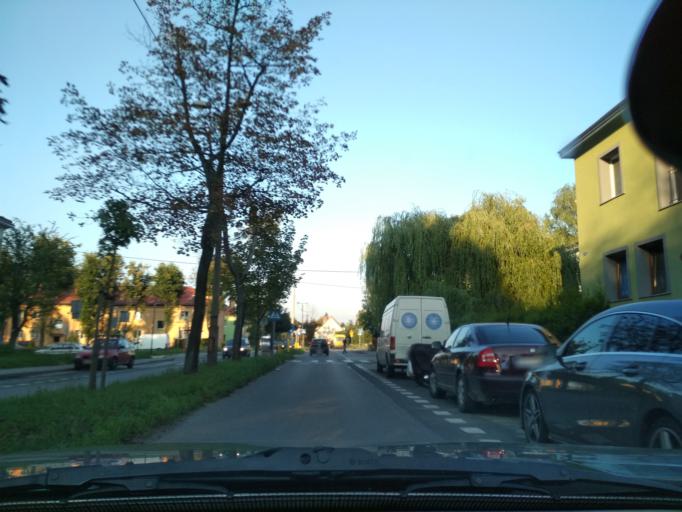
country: PL
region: Silesian Voivodeship
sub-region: Gliwice
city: Gliwice
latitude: 50.2766
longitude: 18.6642
